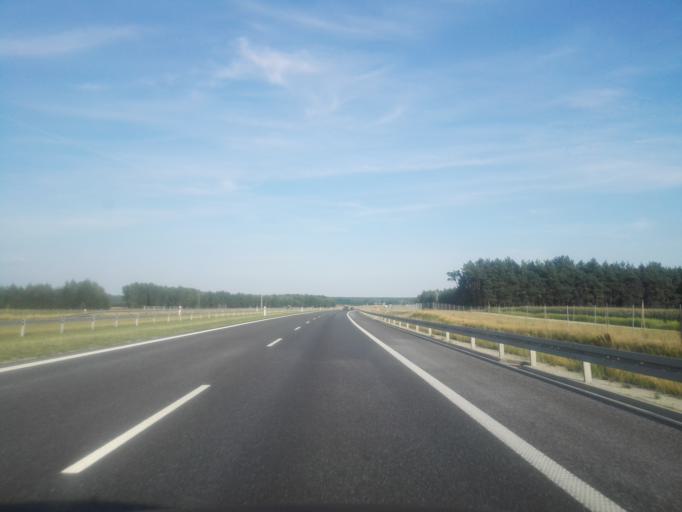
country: PL
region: Lodz Voivodeship
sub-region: Powiat wieruszowski
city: Wieruszow
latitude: 51.3350
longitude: 18.1370
